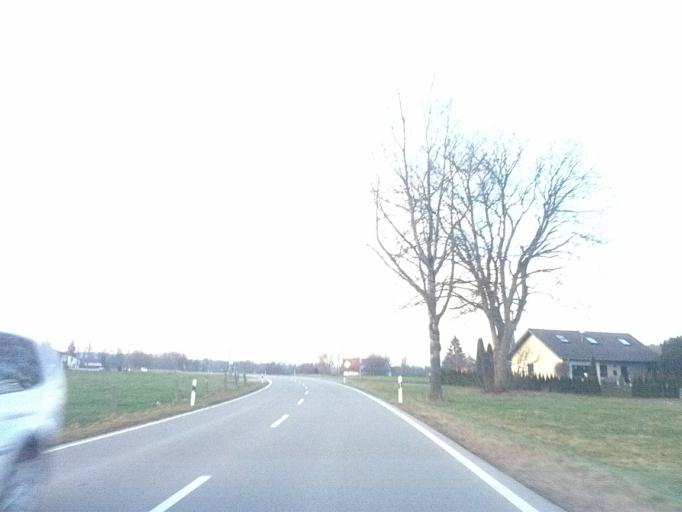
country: DE
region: Bavaria
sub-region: Swabia
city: Lautrach
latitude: 47.9152
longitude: 10.1137
